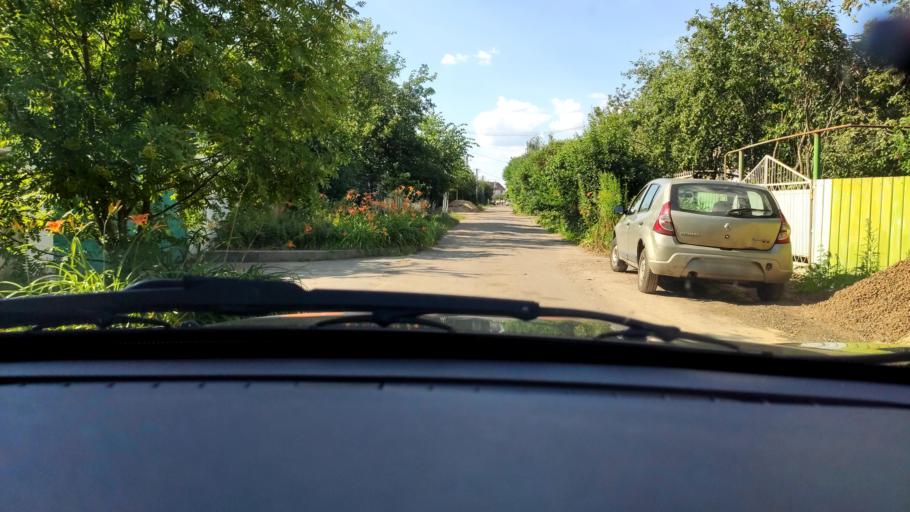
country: RU
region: Voronezj
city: Ramon'
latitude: 51.8322
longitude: 39.2670
